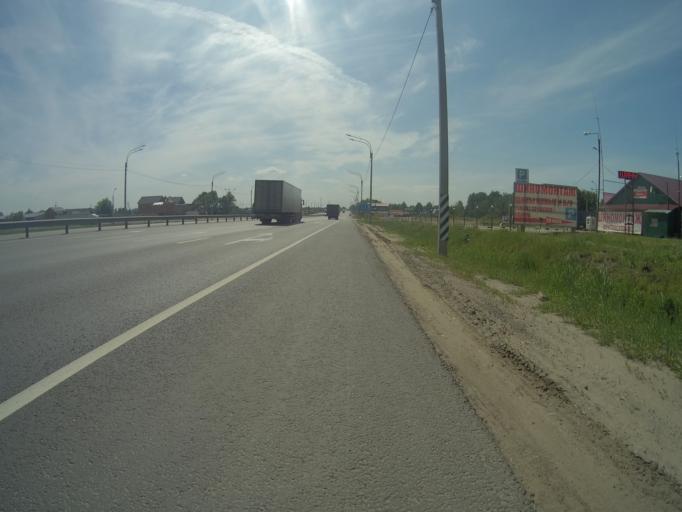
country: RU
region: Vladimir
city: Vorsha
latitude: 56.0690
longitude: 40.1542
